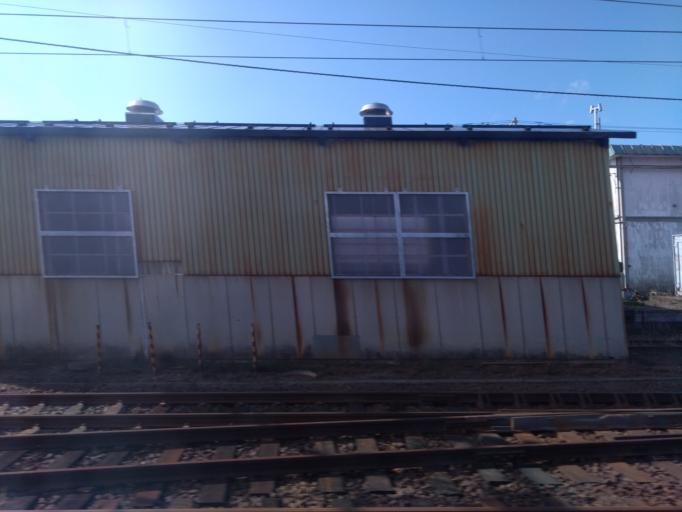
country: JP
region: Hokkaido
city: Kitahiroshima
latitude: 42.9187
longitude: 141.5735
